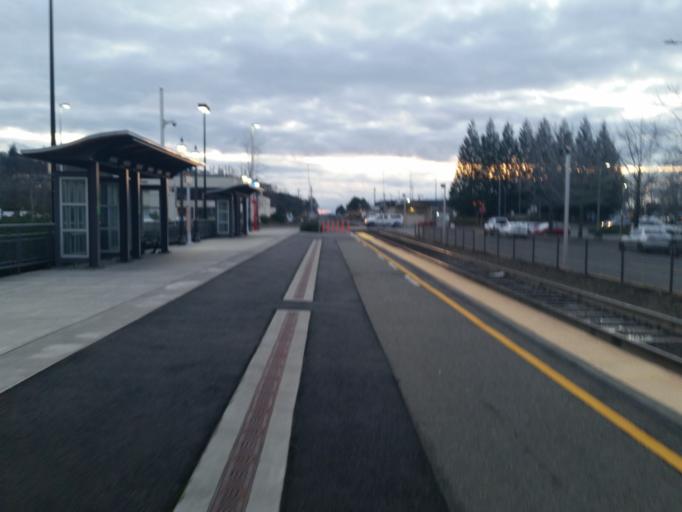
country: US
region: Washington
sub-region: Snohomish County
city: Edmonds
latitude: 47.8105
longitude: -122.3854
